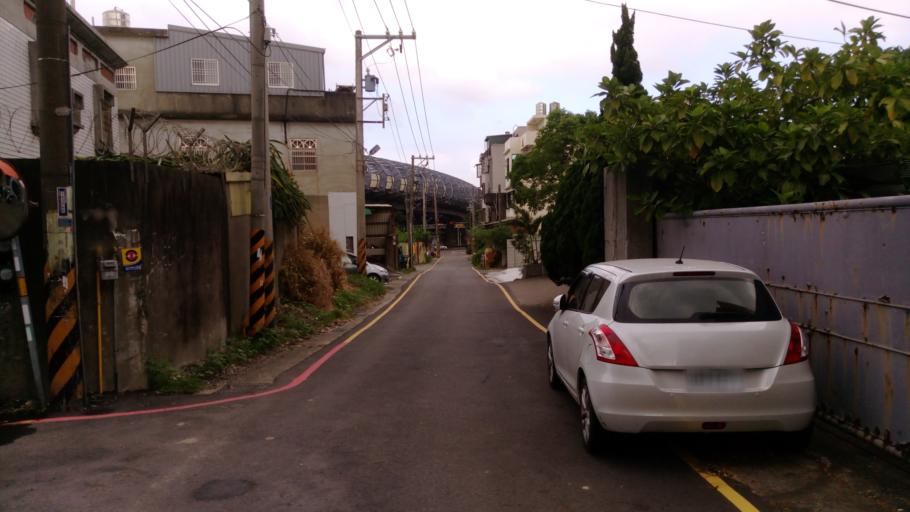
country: TW
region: Taiwan
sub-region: Hsinchu
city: Hsinchu
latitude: 24.7934
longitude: 120.9489
